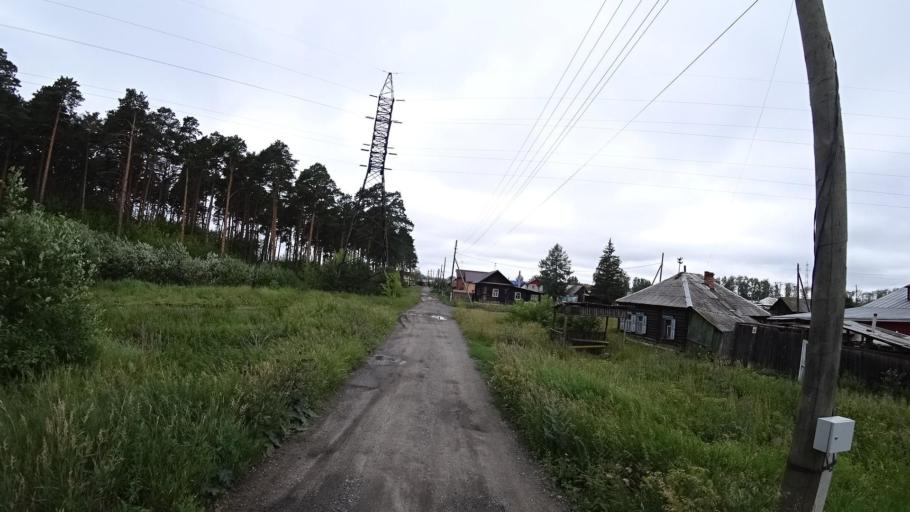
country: RU
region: Sverdlovsk
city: Kamyshlov
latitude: 56.8426
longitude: 62.7502
